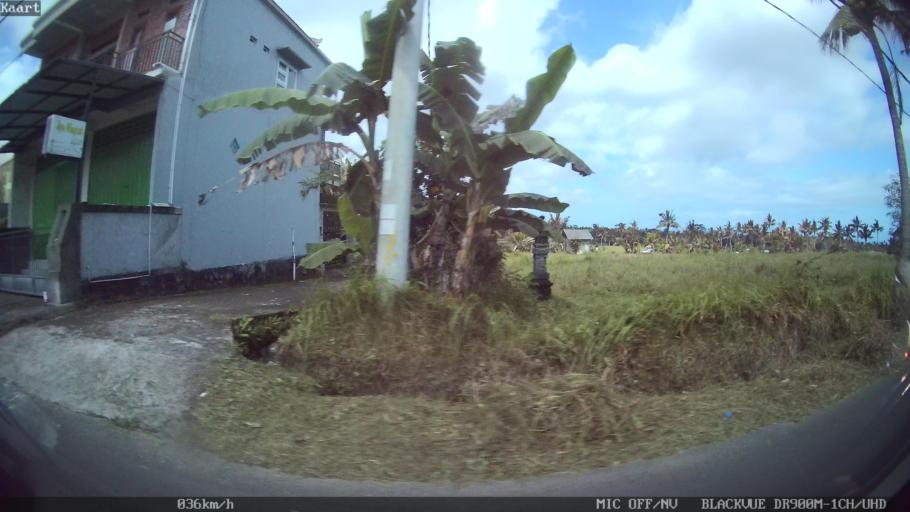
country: ID
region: Bali
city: Banjar Pesalakan
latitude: -8.5162
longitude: 115.3122
